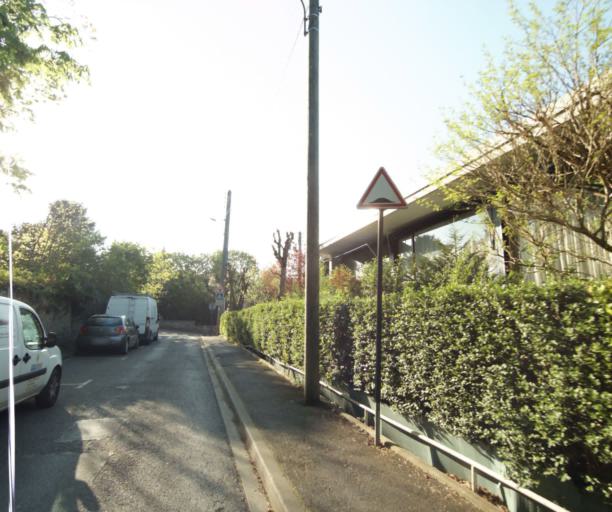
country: FR
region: Ile-de-France
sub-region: Departement des Hauts-de-Seine
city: Ville-d'Avray
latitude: 48.8241
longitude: 2.1981
